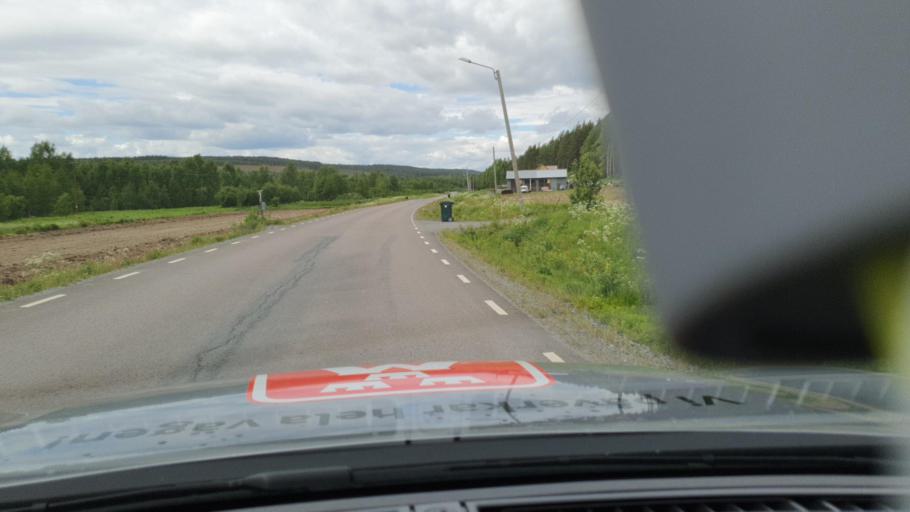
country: SE
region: Norrbotten
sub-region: Lulea Kommun
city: Sodra Sunderbyn
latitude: 65.8395
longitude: 21.9403
